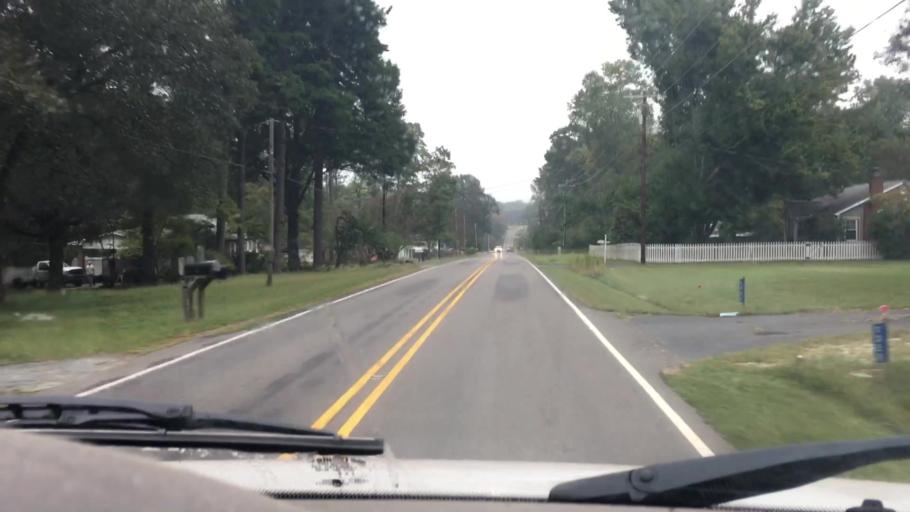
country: US
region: North Carolina
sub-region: Iredell County
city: Mooresville
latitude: 35.6301
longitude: -80.7790
